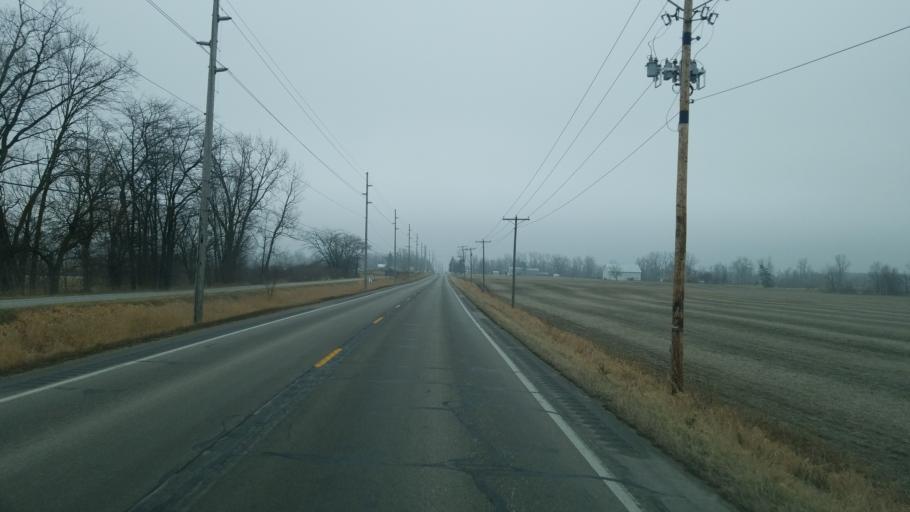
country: US
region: Indiana
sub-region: Adams County
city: Geneva
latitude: 40.5758
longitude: -84.9586
